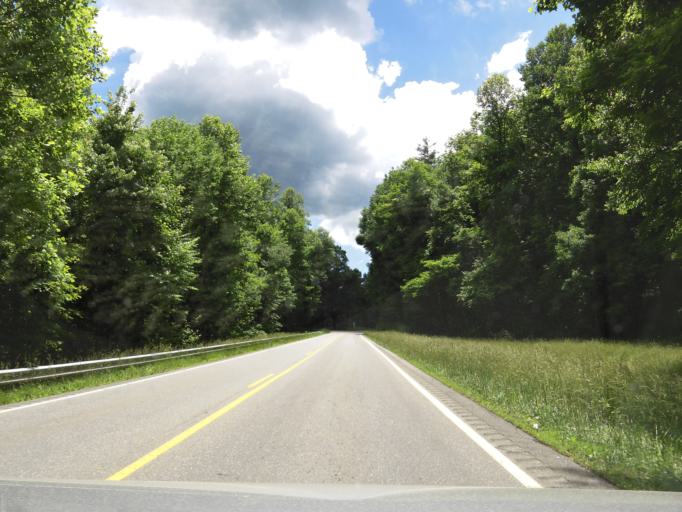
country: US
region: North Carolina
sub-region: Graham County
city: Robbinsville
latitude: 35.2578
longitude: -83.6994
